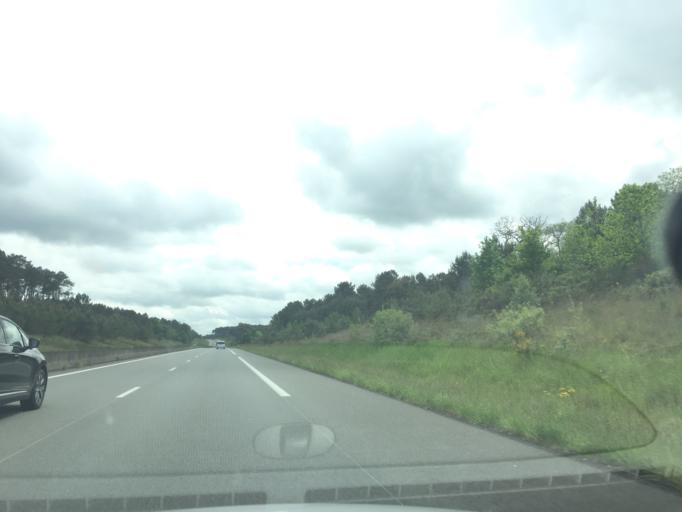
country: FR
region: Pays de la Loire
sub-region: Departement de la Sarthe
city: Mayet
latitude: 47.7629
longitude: 0.3143
